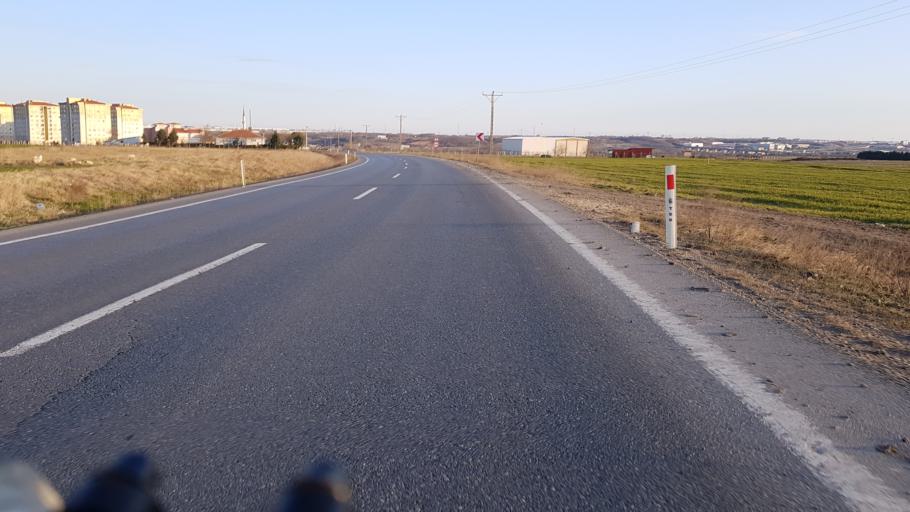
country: TR
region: Tekirdag
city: Velimese
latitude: 41.2560
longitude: 27.8616
